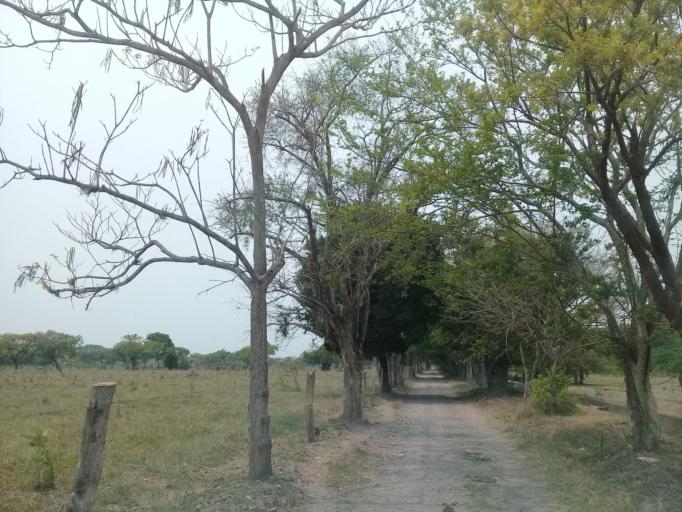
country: MX
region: Veracruz
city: Jamapa
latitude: 18.9242
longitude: -96.2013
